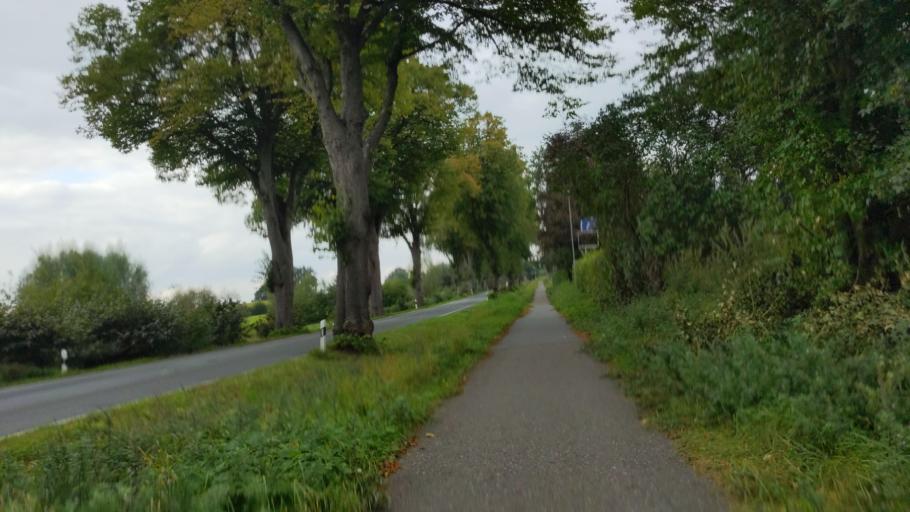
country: DE
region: Schleswig-Holstein
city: Krummesse
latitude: 53.7919
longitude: 10.6388
